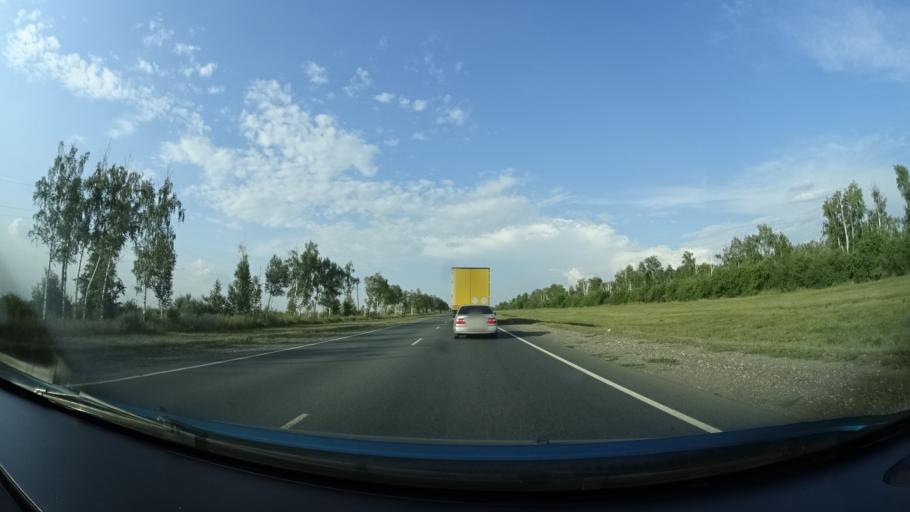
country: RU
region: Samara
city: Krasnyy Yar
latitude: 53.6625
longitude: 50.7564
